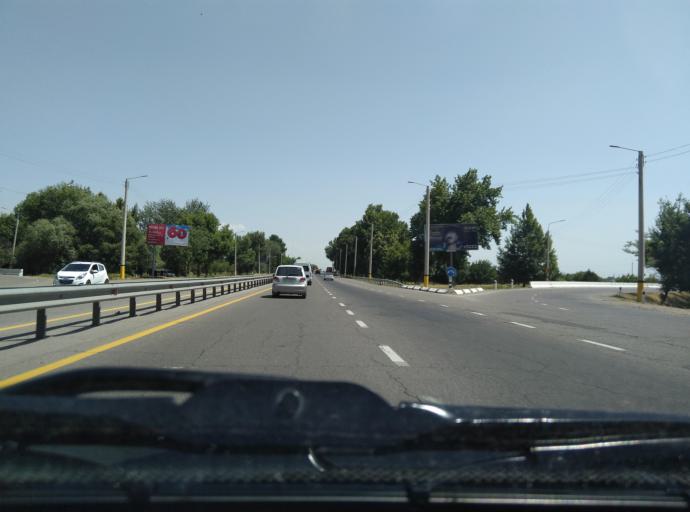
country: UZ
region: Toshkent Shahri
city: Bektemir
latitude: 41.2440
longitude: 69.3968
